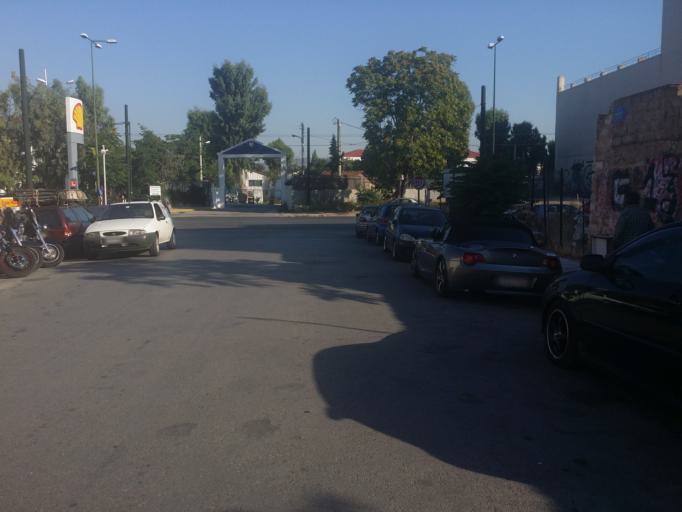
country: GR
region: Attica
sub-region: Nomarchia Athinas
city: Tavros
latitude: 37.9706
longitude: 23.7040
